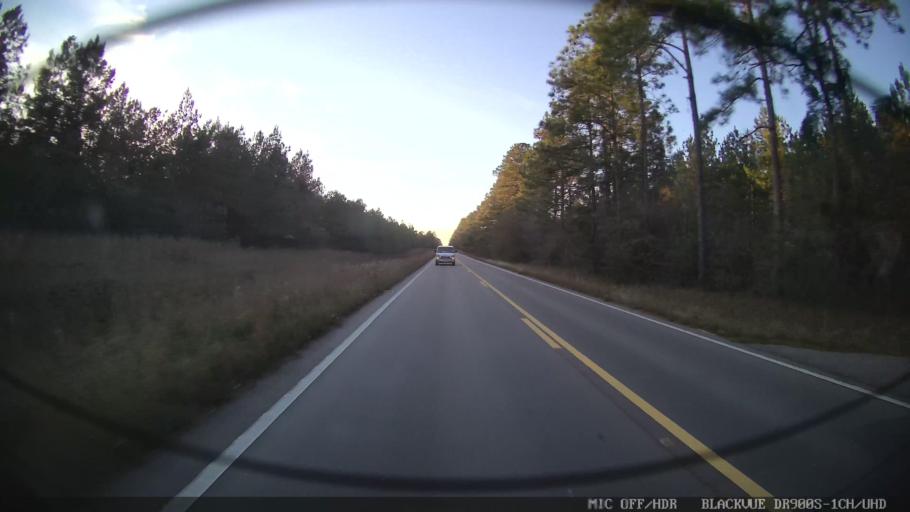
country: US
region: Mississippi
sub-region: Lamar County
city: Lumberton
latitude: 30.9954
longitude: -89.2911
